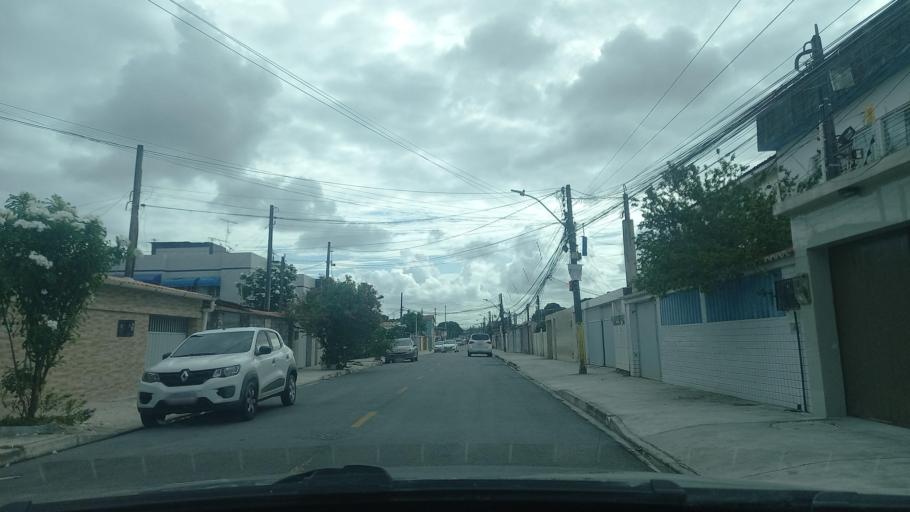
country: BR
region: Pernambuco
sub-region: Recife
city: Recife
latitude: -8.1076
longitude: -34.9183
